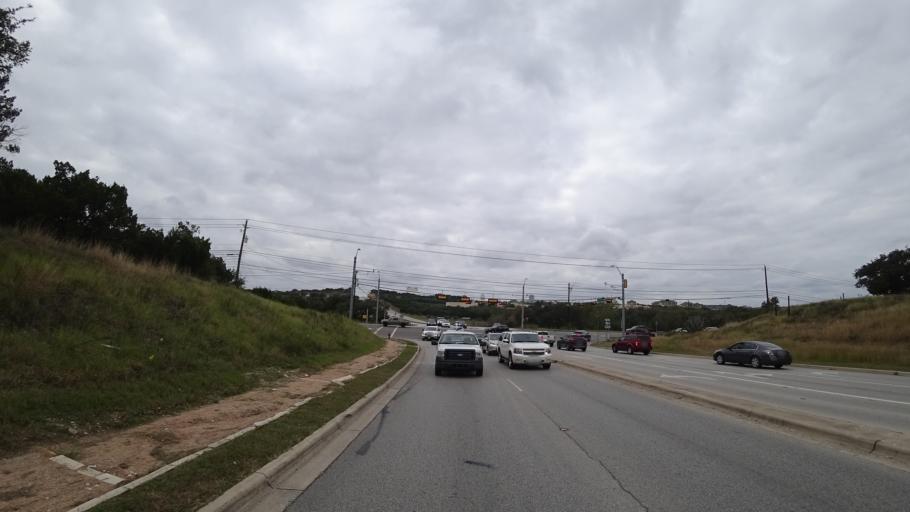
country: US
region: Texas
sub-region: Travis County
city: Bee Cave
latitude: 30.3165
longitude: -97.9490
